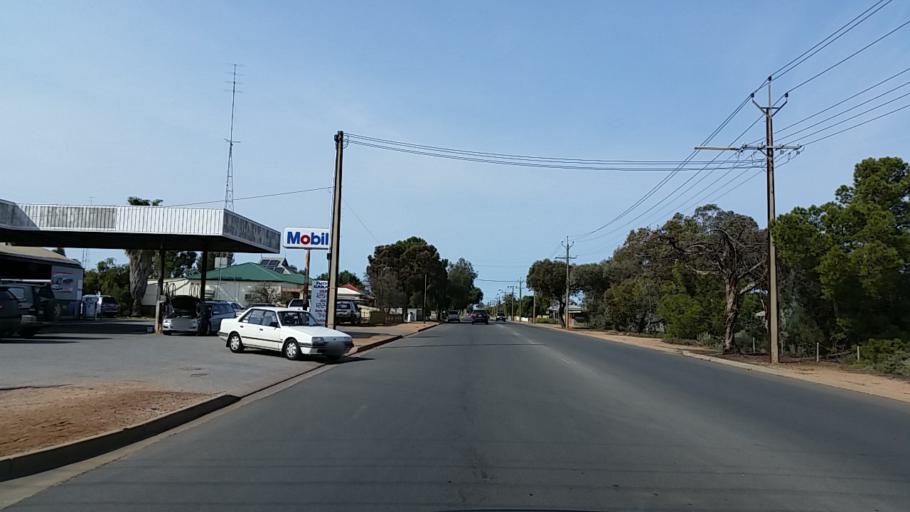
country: AU
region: South Australia
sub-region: Port Pirie City and Dists
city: Port Pirie
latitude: -33.1872
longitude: 137.9976
